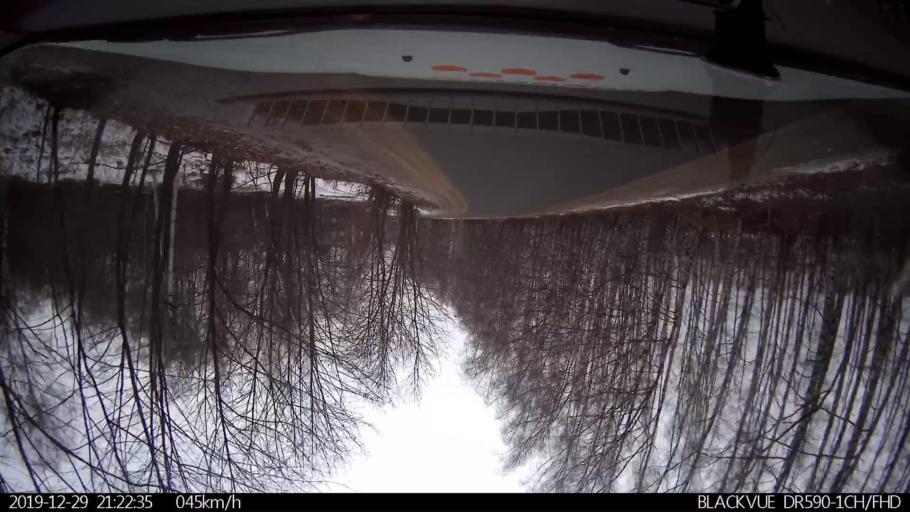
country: RU
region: Nizjnij Novgorod
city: Afonino
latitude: 56.2161
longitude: 44.0345
